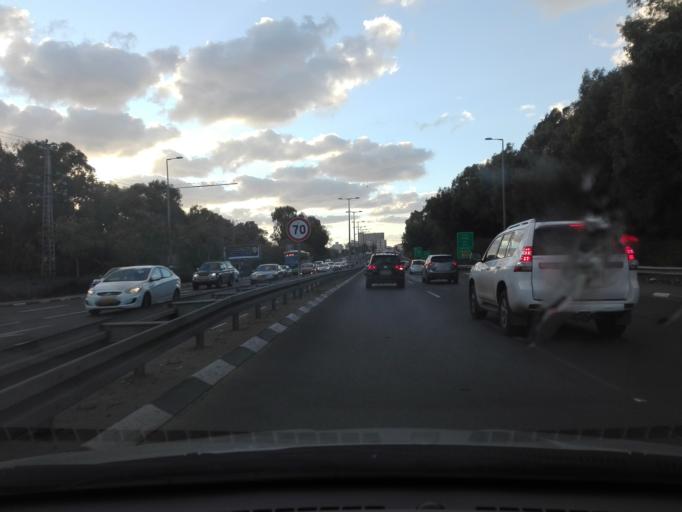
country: IL
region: Central District
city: Bet Yizhaq
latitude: 32.3243
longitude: 34.8745
